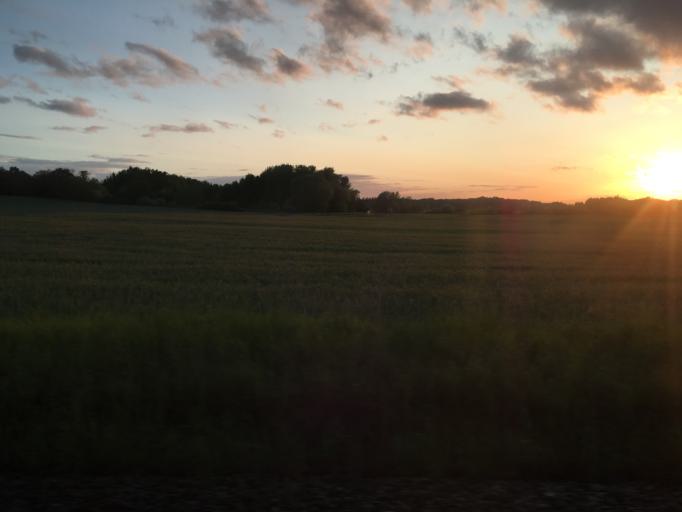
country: DE
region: Brandenburg
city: Rangsdorf
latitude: 52.2758
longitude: 13.4367
